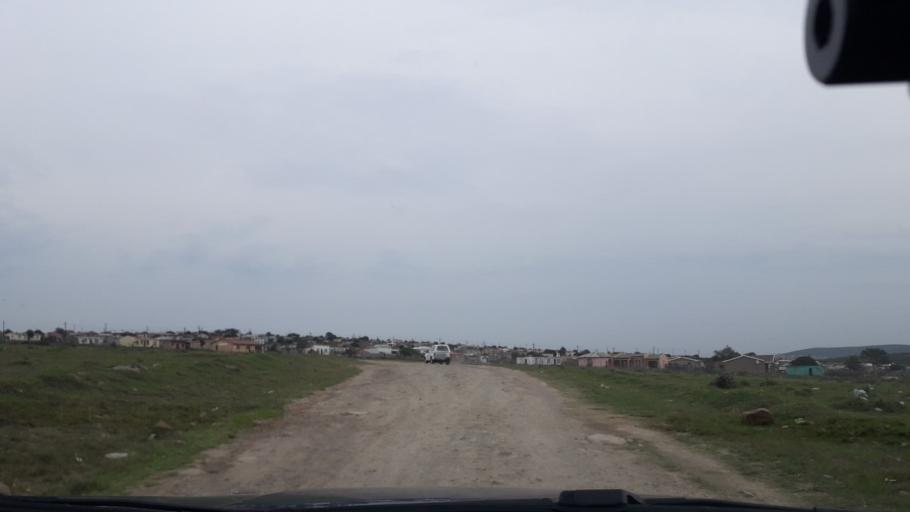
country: ZA
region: Eastern Cape
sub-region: Buffalo City Metropolitan Municipality
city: Bhisho
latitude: -32.8328
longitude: 27.3746
